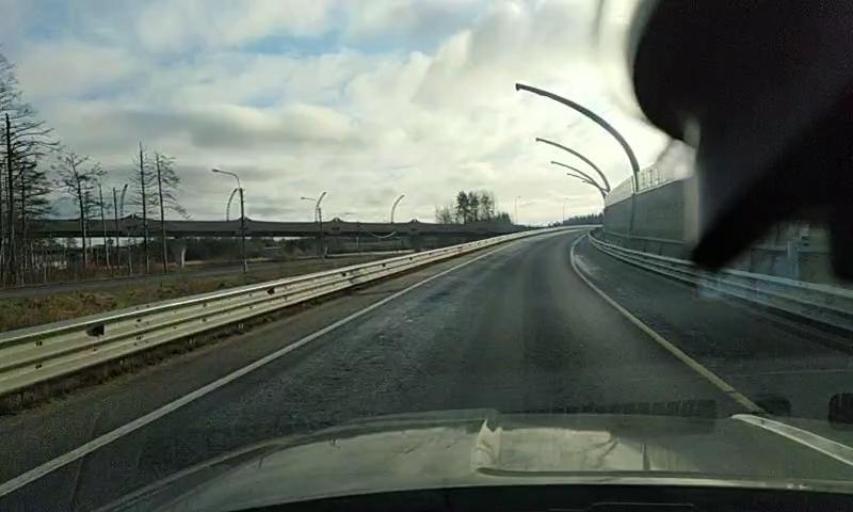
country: RU
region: St.-Petersburg
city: Solnechnoye
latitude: 60.1518
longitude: 29.9707
